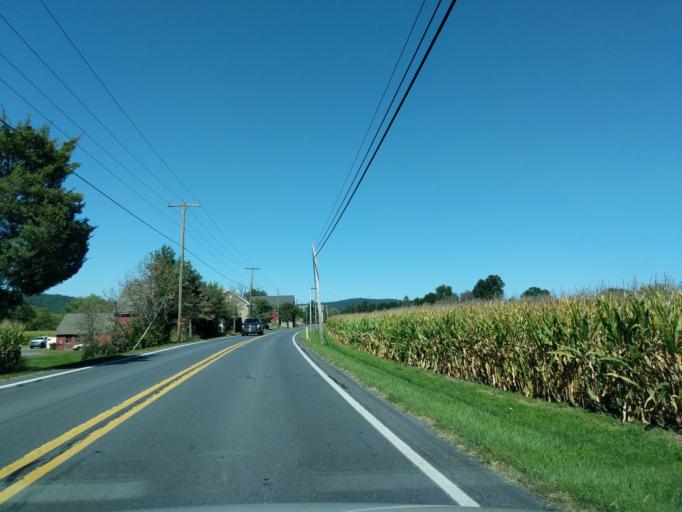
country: US
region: Pennsylvania
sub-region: Lehigh County
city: Emmaus
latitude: 40.5206
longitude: -75.4494
